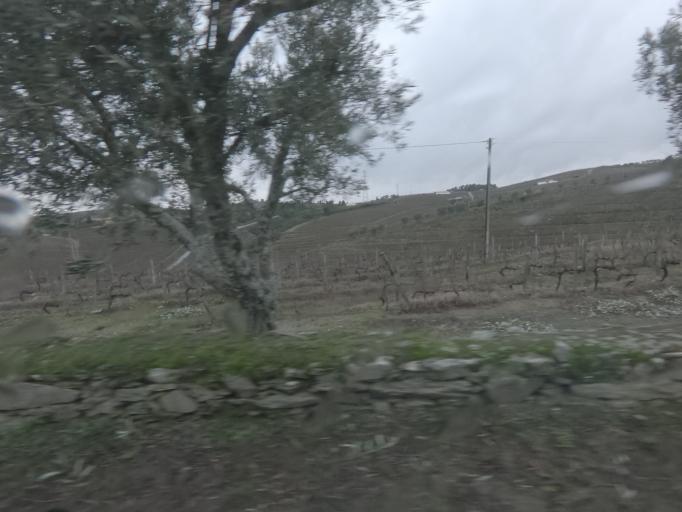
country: PT
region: Viseu
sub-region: Armamar
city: Armamar
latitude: 41.1651
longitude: -7.7026
